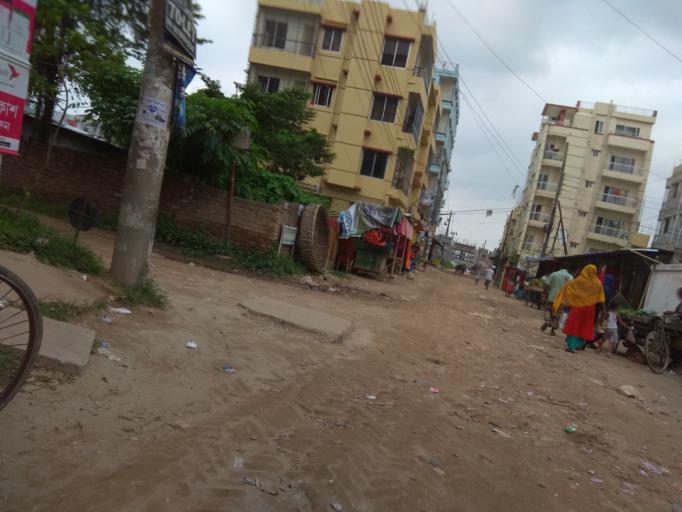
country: BD
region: Dhaka
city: Tungi
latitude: 23.8280
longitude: 90.3498
